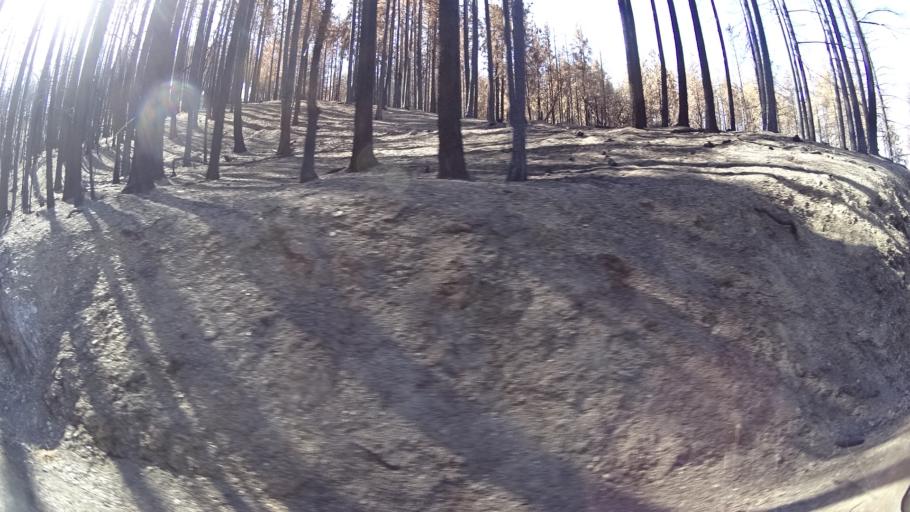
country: US
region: California
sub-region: Tehama County
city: Rancho Tehama Reserve
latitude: 39.6668
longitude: -122.7074
